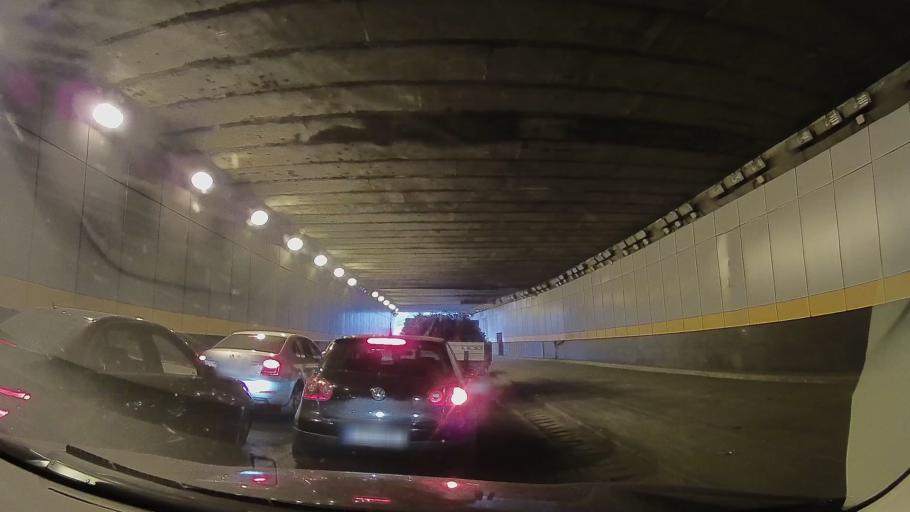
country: RO
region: Bucuresti
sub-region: Municipiul Bucuresti
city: Bucharest
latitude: 44.4474
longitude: 26.1243
